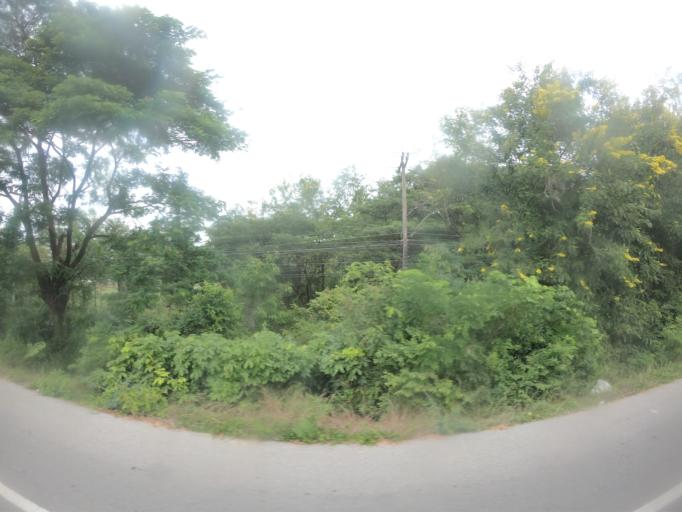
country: TH
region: Maha Sarakham
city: Maha Sarakham
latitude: 16.1469
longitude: 103.4083
